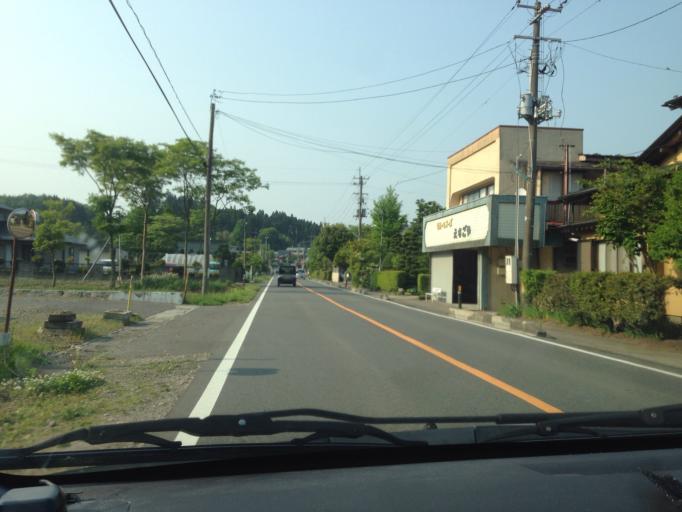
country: JP
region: Tochigi
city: Kuroiso
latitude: 37.0770
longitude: 140.1910
